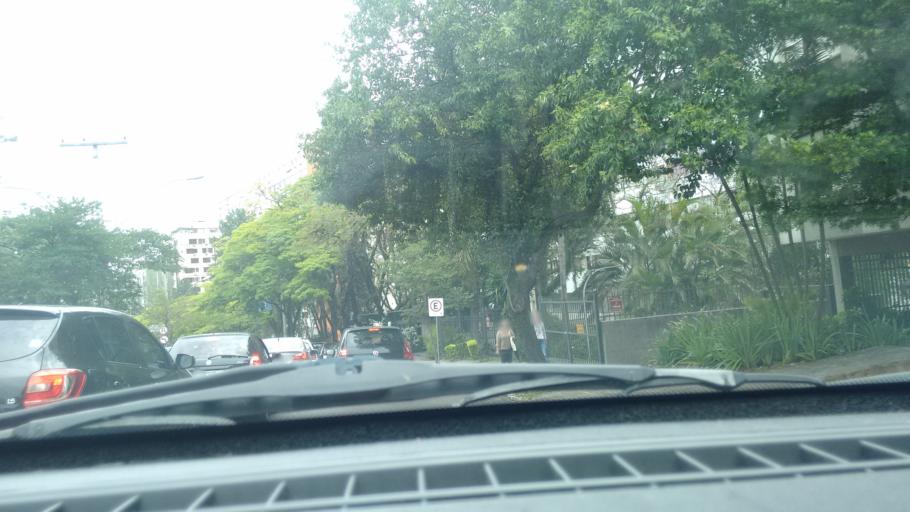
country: BR
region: Rio Grande do Sul
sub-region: Porto Alegre
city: Porto Alegre
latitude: -30.0302
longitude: -51.1828
